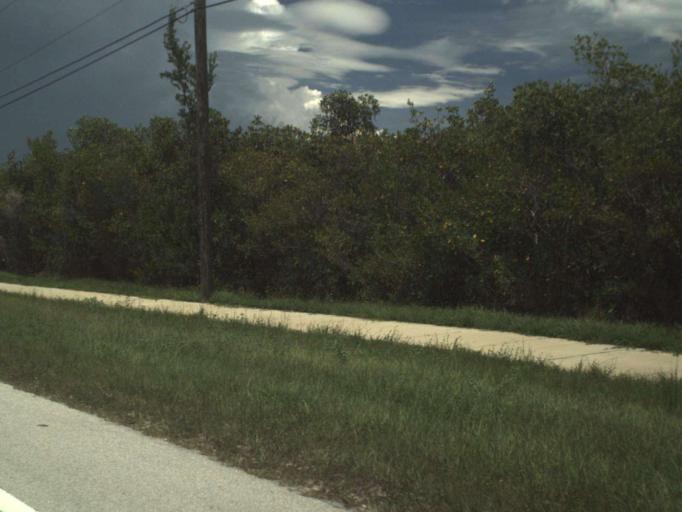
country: US
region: Florida
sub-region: Saint Lucie County
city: Indian River Estates
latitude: 27.4139
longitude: -80.2740
